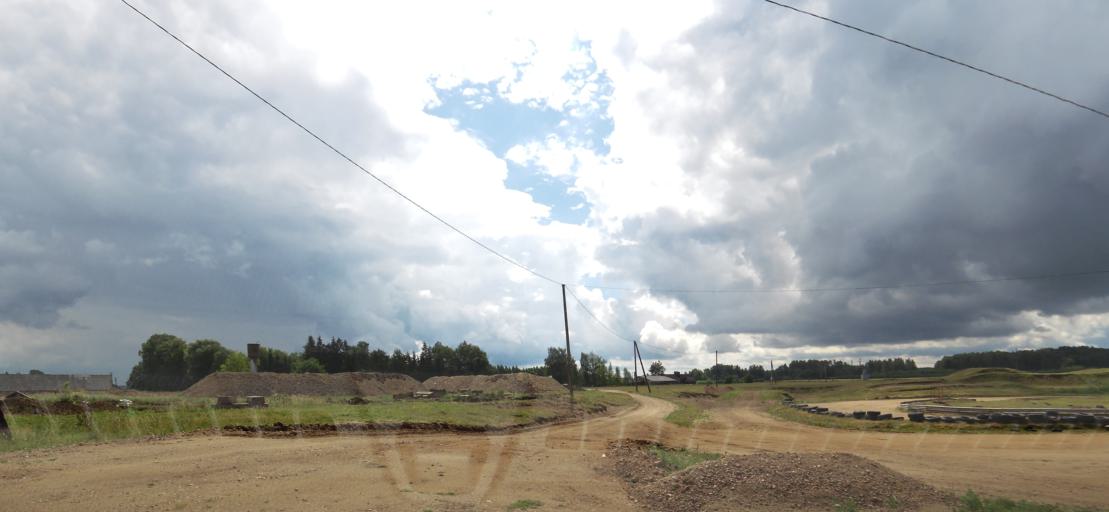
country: LT
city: Vabalninkas
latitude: 55.8889
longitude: 24.7754
